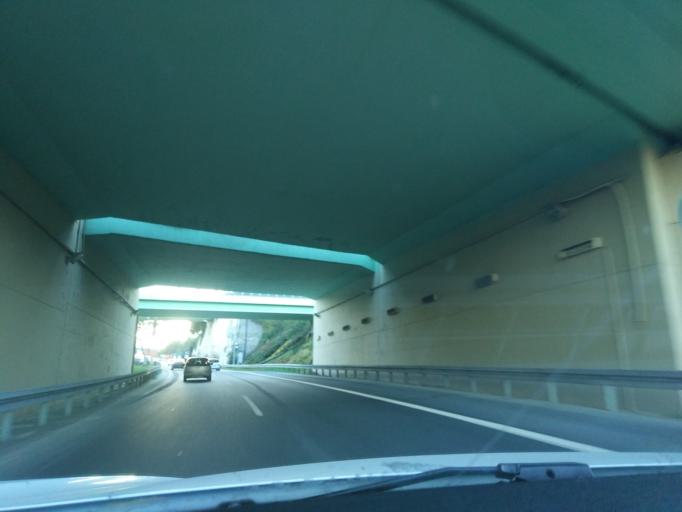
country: TR
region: Istanbul
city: Sisli
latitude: 41.0580
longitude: 29.0186
